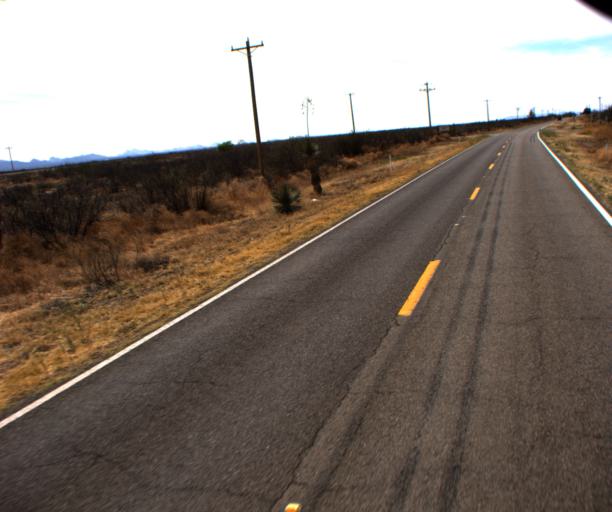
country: US
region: Arizona
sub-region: Cochise County
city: Bisbee
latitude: 31.7307
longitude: -109.6871
